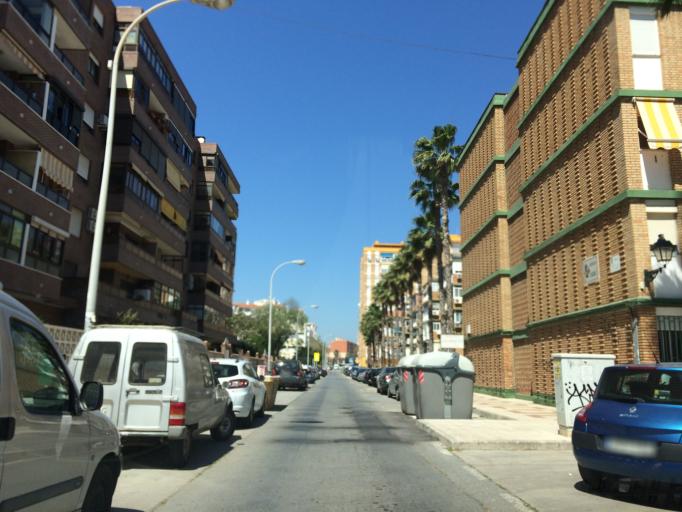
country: ES
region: Andalusia
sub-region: Provincia de Malaga
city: Malaga
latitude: 36.6891
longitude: -4.4529
